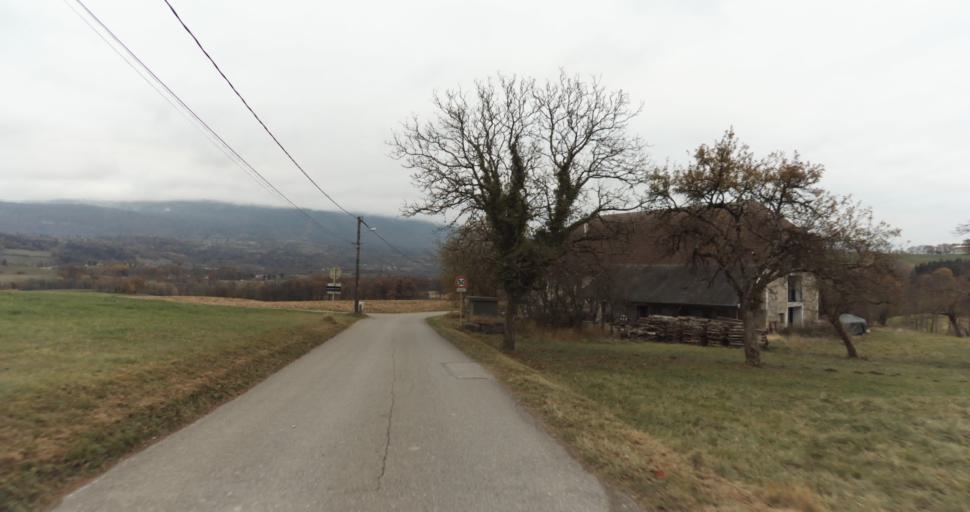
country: FR
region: Rhone-Alpes
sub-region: Departement de la Haute-Savoie
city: Chavanod
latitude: 45.8543
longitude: 6.0458
